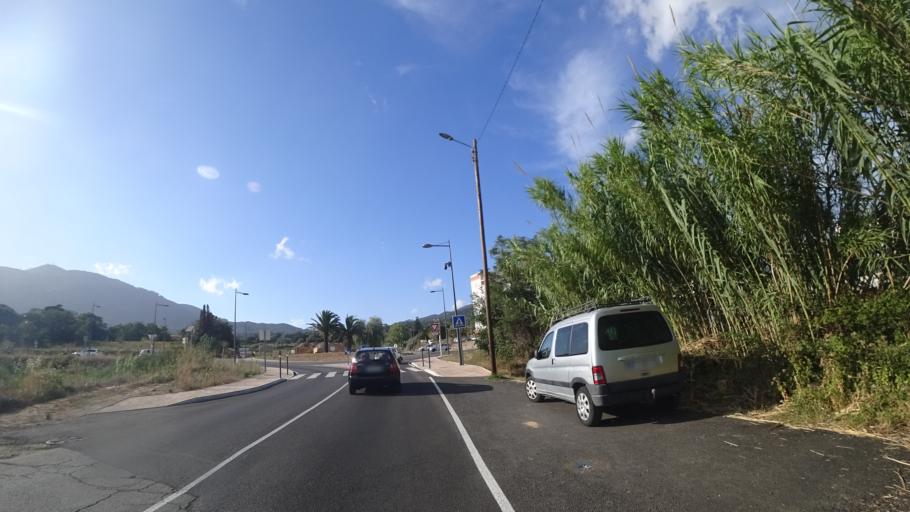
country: FR
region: Corsica
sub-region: Departement de la Corse-du-Sud
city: Ajaccio
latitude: 41.9383
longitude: 8.7422
